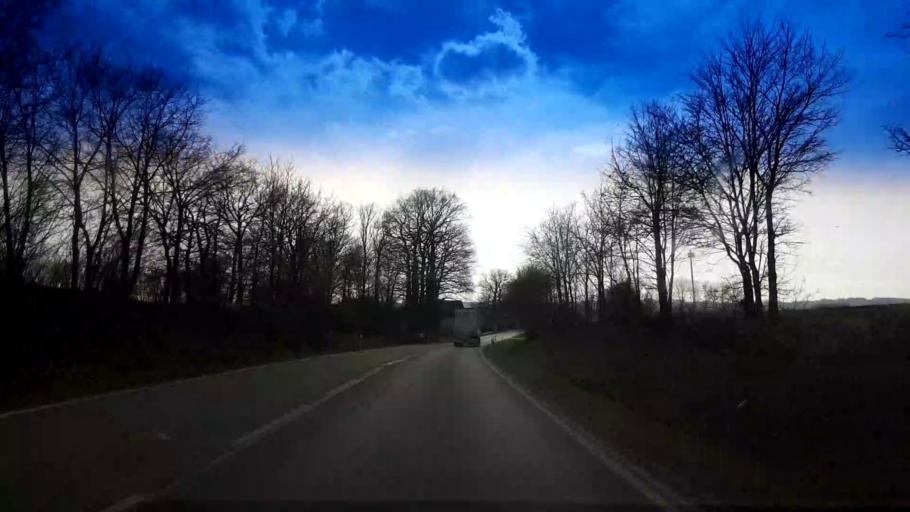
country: DE
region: Bavaria
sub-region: Upper Franconia
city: Gesees
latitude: 50.0288
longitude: 11.6498
